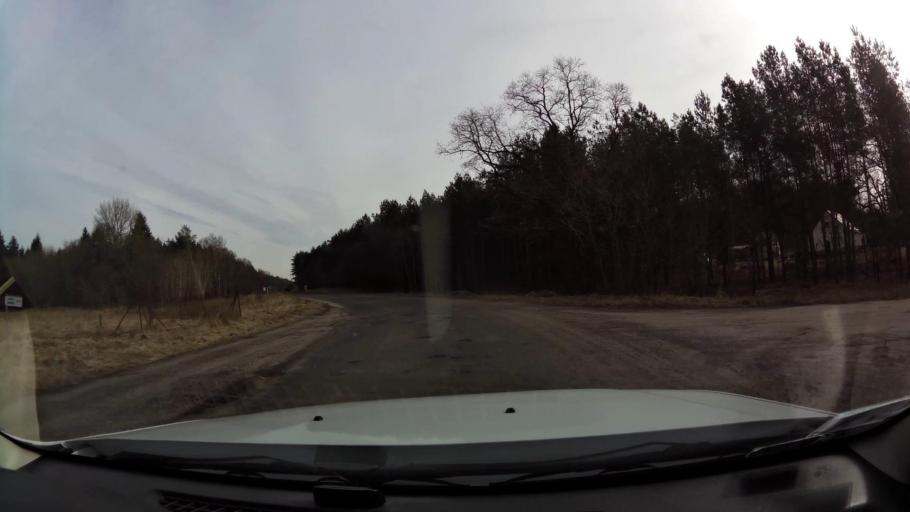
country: PL
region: West Pomeranian Voivodeship
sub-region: Powiat drawski
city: Drawsko Pomorskie
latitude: 53.4700
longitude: 15.6964
